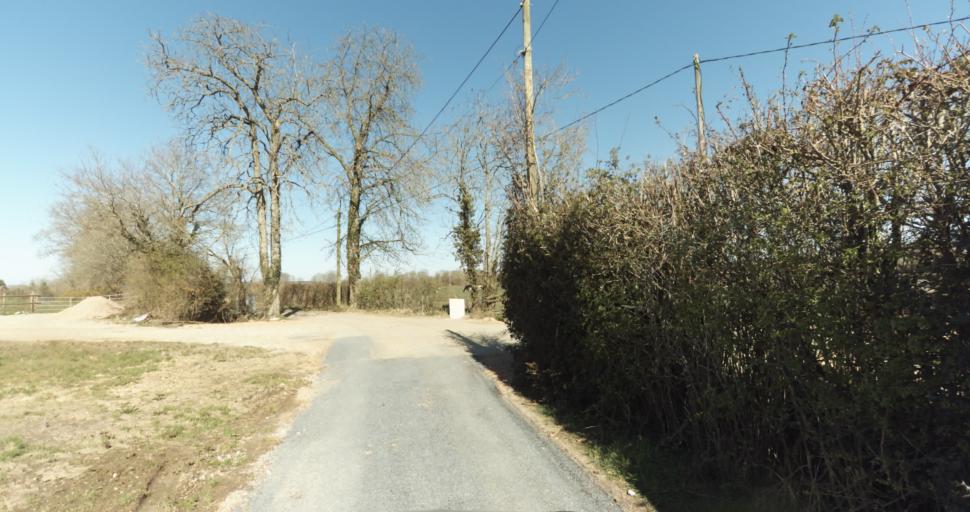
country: FR
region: Lower Normandy
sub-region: Departement du Calvados
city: Livarot
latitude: 48.9789
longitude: 0.0871
